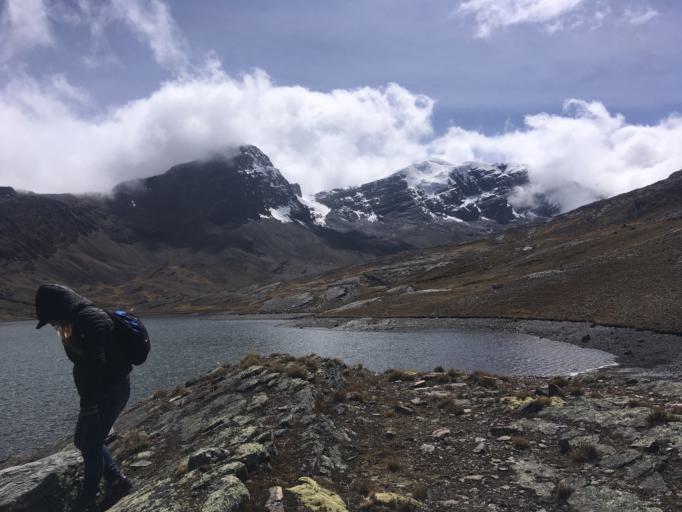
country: BO
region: La Paz
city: La Paz
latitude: -16.3973
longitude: -67.9697
